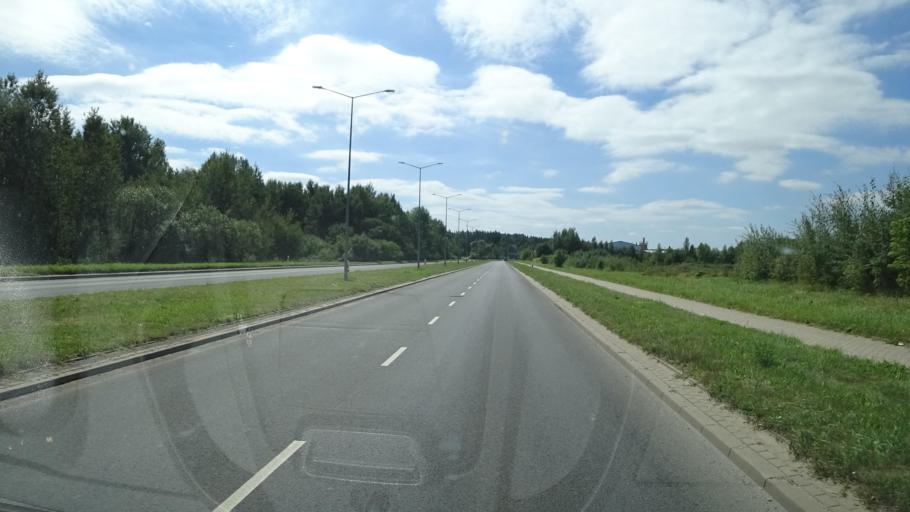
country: PL
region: Warmian-Masurian Voivodeship
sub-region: Powiat elcki
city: Elk
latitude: 53.8234
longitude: 22.3901
